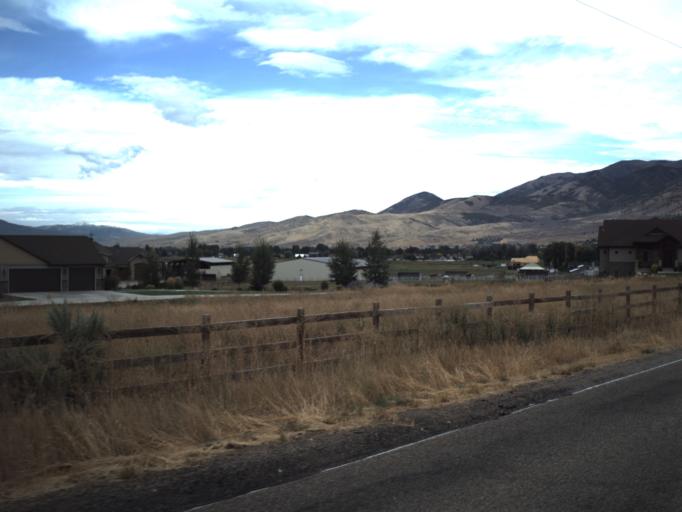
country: US
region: Utah
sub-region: Morgan County
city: Morgan
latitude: 41.0186
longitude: -111.6758
